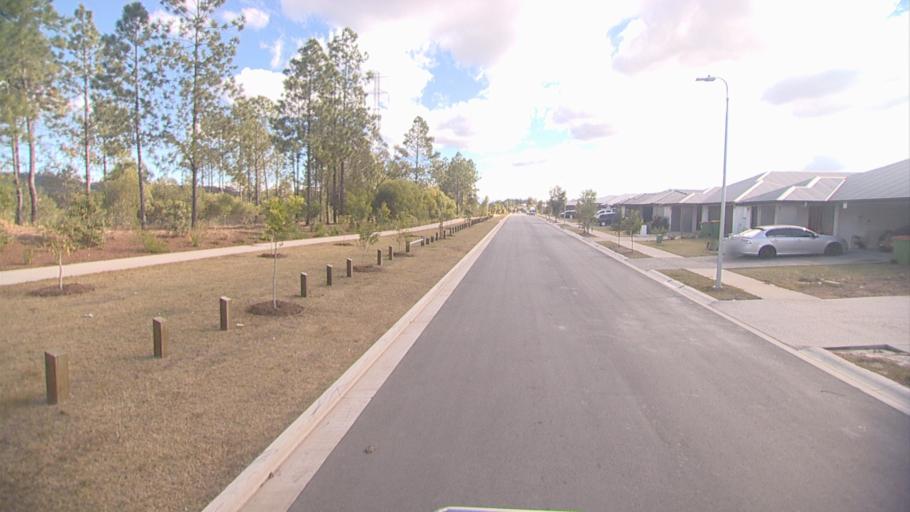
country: AU
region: Queensland
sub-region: Logan
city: Chambers Flat
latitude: -27.8117
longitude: 153.1142
